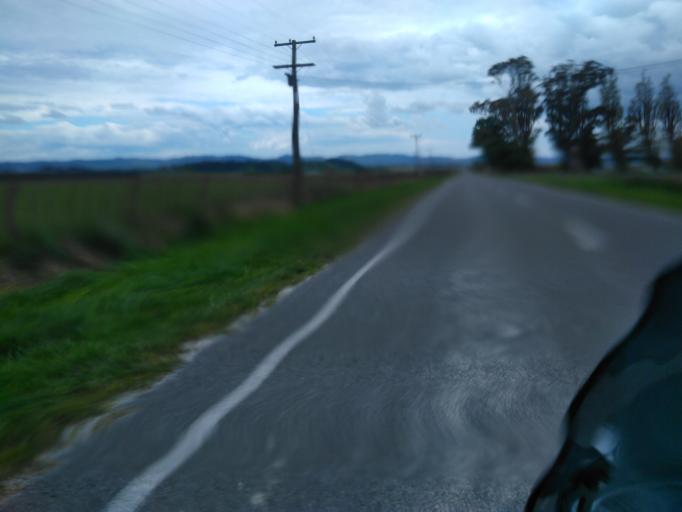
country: NZ
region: Gisborne
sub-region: Gisborne District
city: Gisborne
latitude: -38.6457
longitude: 177.8554
